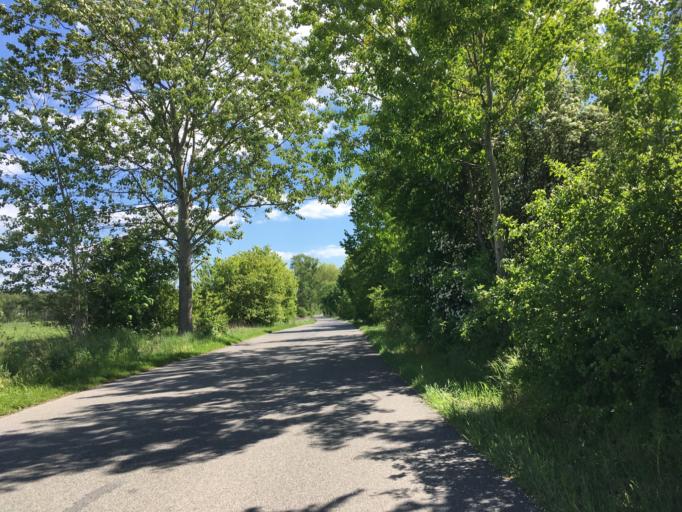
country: DE
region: Brandenburg
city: Rudnitz
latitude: 52.7022
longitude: 13.6638
